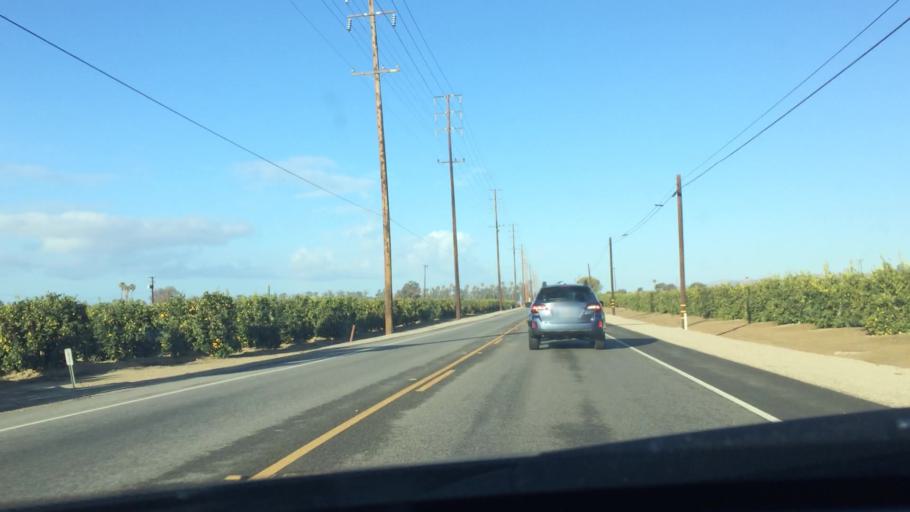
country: US
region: California
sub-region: Ventura County
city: Camarillo
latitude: 34.2637
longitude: -119.0676
